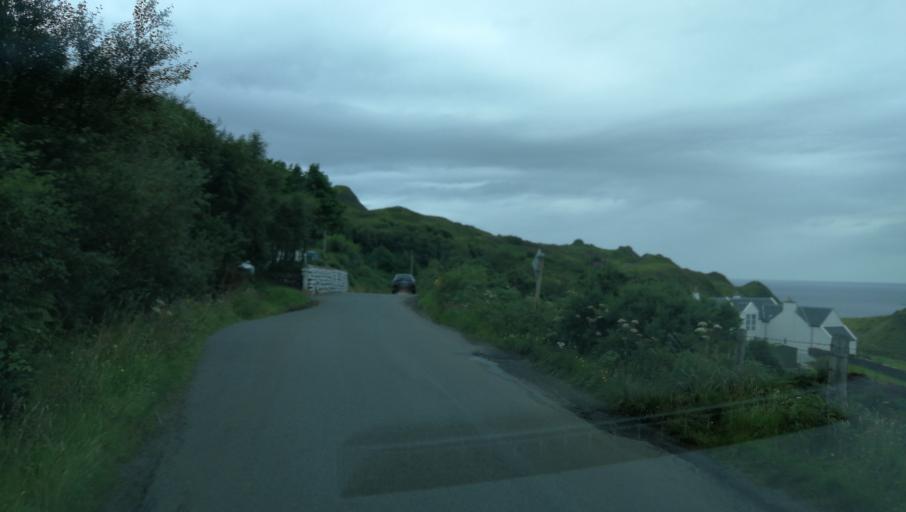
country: GB
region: Scotland
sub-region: Highland
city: Portree
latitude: 57.6473
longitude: -6.2436
